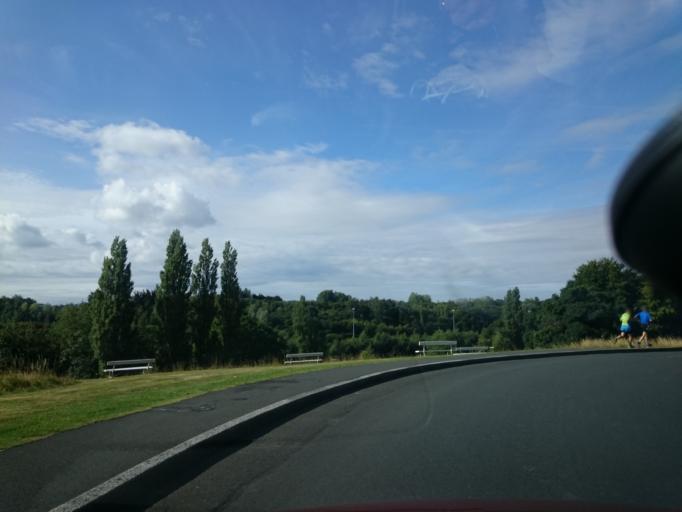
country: IE
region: Leinster
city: Chapelizod
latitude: 53.3468
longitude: -6.3286
